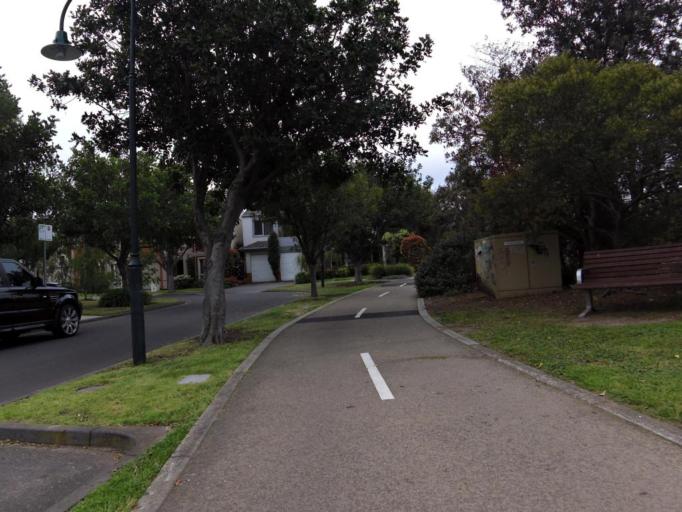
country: AU
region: Victoria
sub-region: Port Phillip
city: Port Melbourne
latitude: -37.8394
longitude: 144.9338
